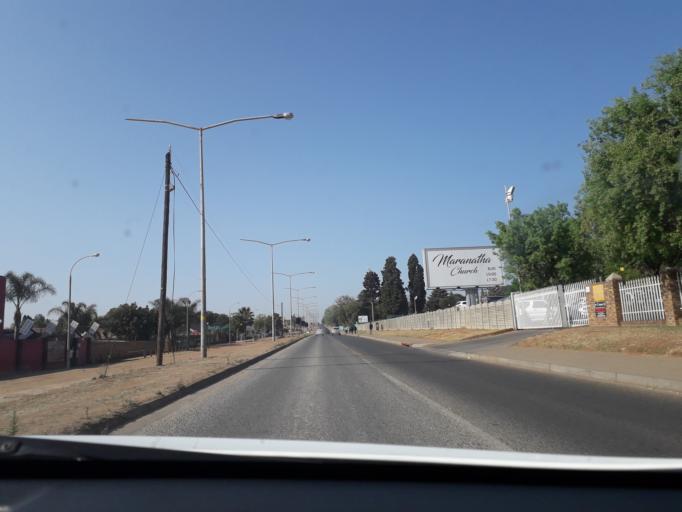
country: ZA
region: Gauteng
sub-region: Ekurhuleni Metropolitan Municipality
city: Tembisa
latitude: -26.0724
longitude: 28.2471
